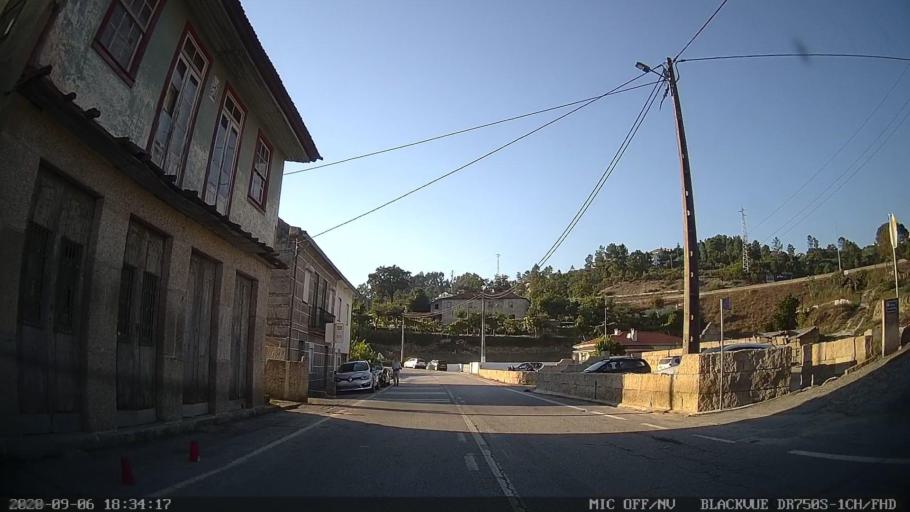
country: PT
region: Porto
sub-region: Amarante
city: Amarante
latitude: 41.2569
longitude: -8.0536
